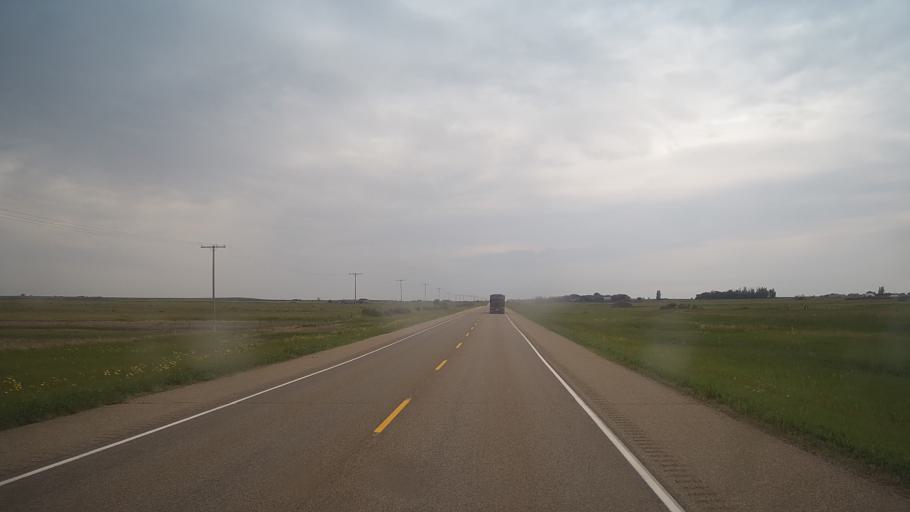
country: CA
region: Saskatchewan
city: Langham
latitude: 52.1289
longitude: -107.1523
